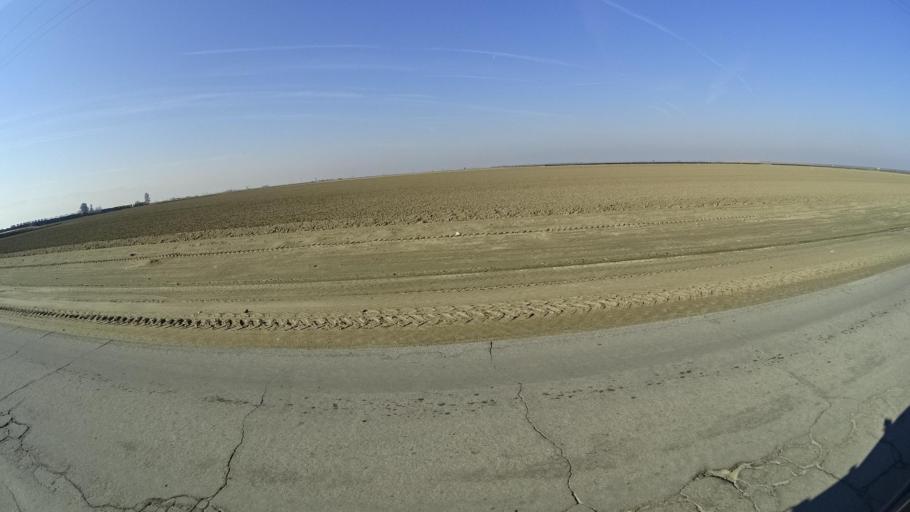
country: US
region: California
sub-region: Kern County
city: Arvin
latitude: 35.1675
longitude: -118.8781
